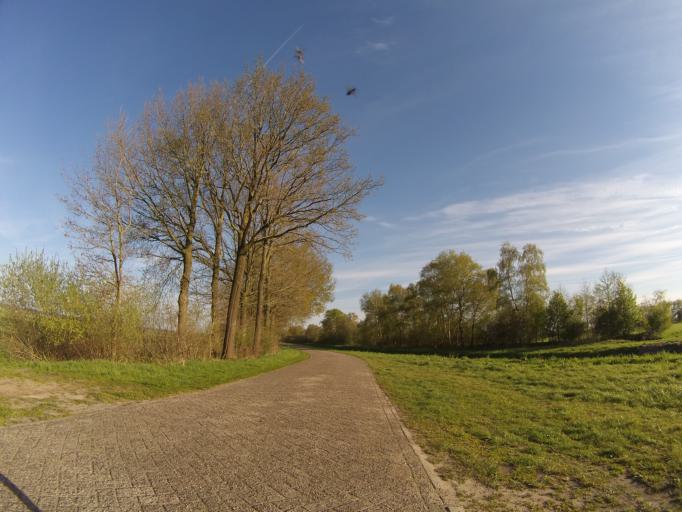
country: NL
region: Drenthe
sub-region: Gemeente Coevorden
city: Sleen
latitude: 52.7537
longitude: 6.7514
